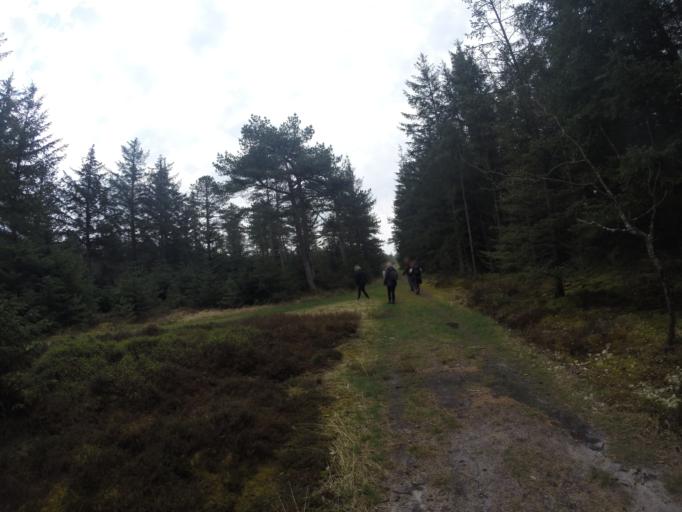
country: DK
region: North Denmark
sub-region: Thisted Kommune
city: Hanstholm
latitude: 57.0417
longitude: 8.5719
